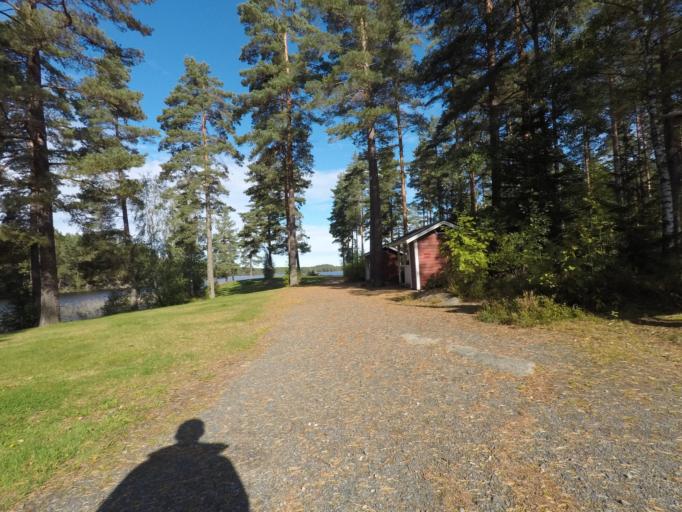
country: SE
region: Vaestmanland
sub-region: Skinnskattebergs Kommun
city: Skinnskatteberg
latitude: 59.8048
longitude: 15.7368
